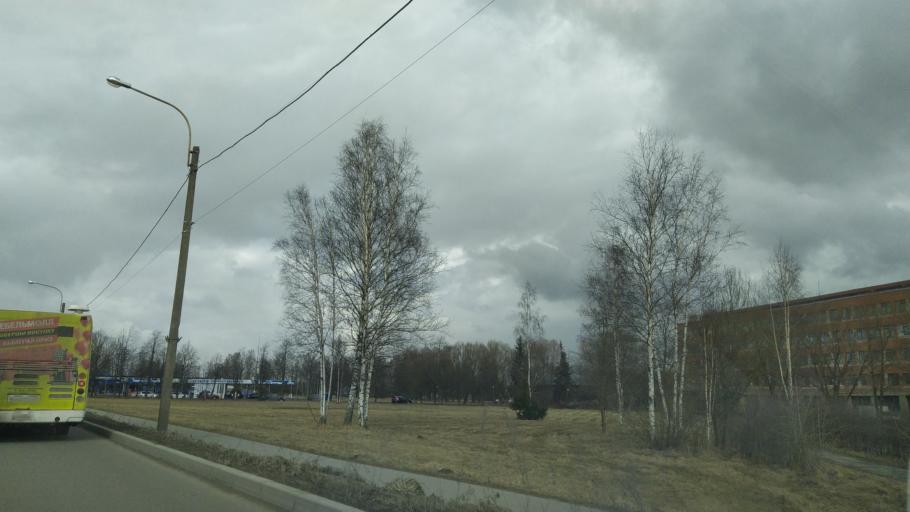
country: RU
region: St.-Petersburg
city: Tyarlevo
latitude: 59.7089
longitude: 30.4372
